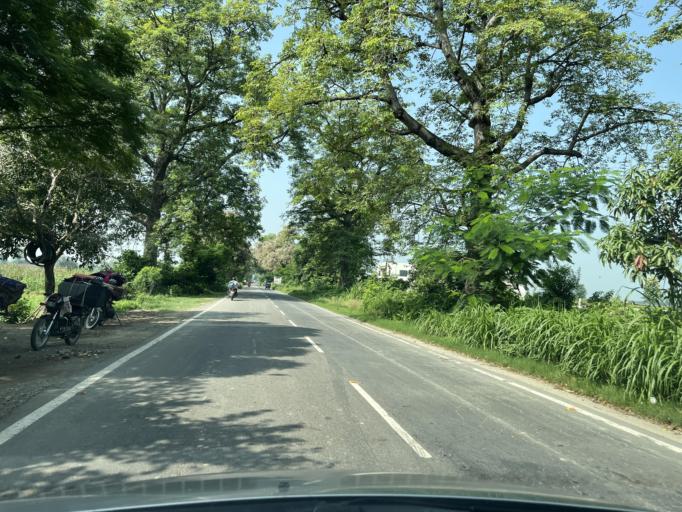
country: IN
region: Uttarakhand
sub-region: Udham Singh Nagar
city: Bazpur
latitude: 29.1898
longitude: 79.1900
